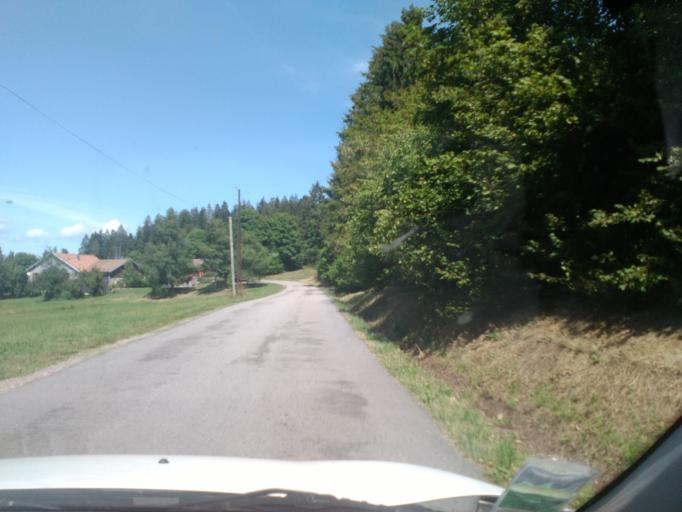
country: FR
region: Lorraine
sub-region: Departement des Vosges
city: Le Tholy
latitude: 48.0382
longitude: 6.7762
